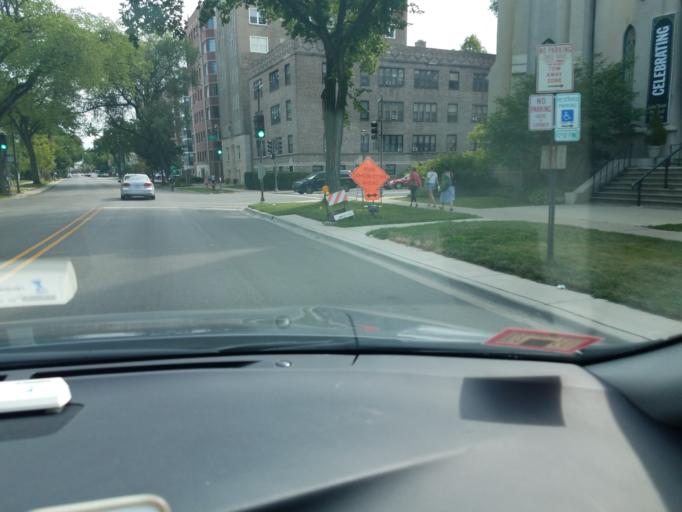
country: US
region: Illinois
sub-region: Cook County
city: Evanston
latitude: 42.0444
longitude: -87.6805
